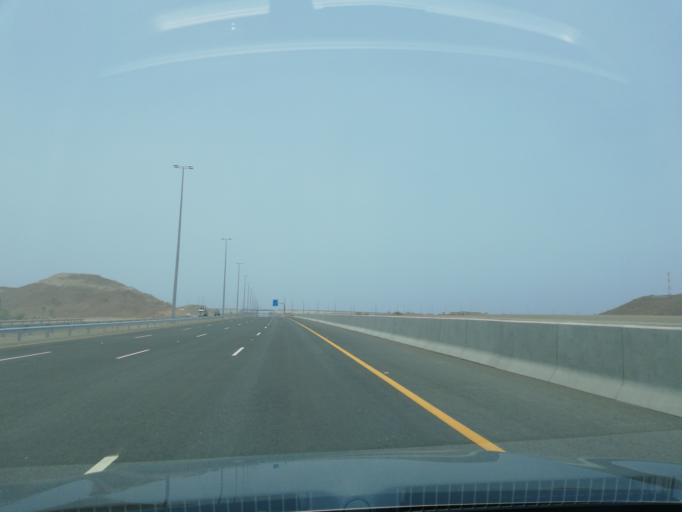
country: OM
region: Al Batinah
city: Al Liwa'
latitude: 24.5203
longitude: 56.5044
